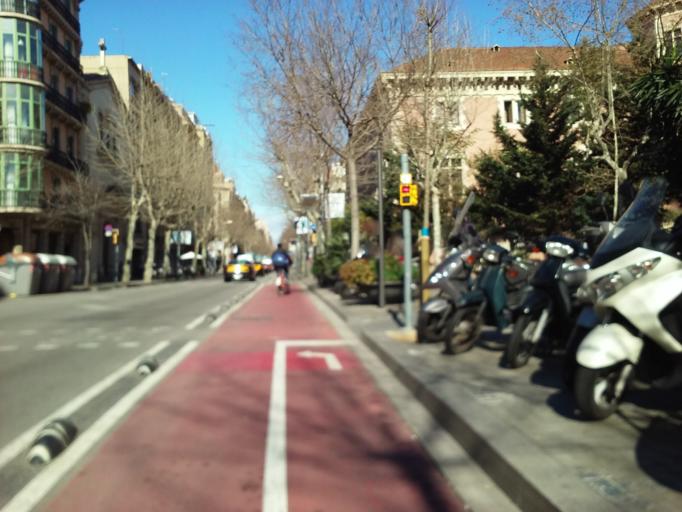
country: ES
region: Catalonia
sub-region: Provincia de Barcelona
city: Eixample
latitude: 41.3881
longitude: 2.1617
